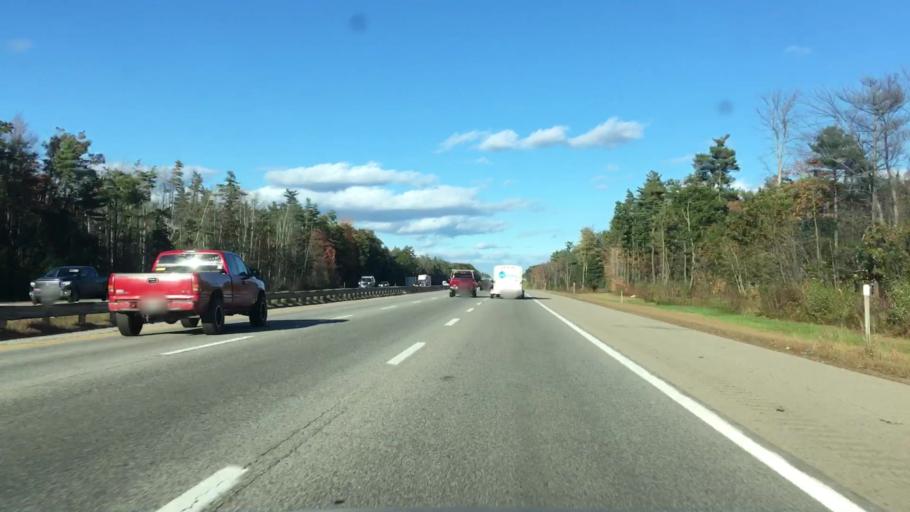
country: US
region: Maine
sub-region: York County
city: Saco
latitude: 43.5450
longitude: -70.4343
